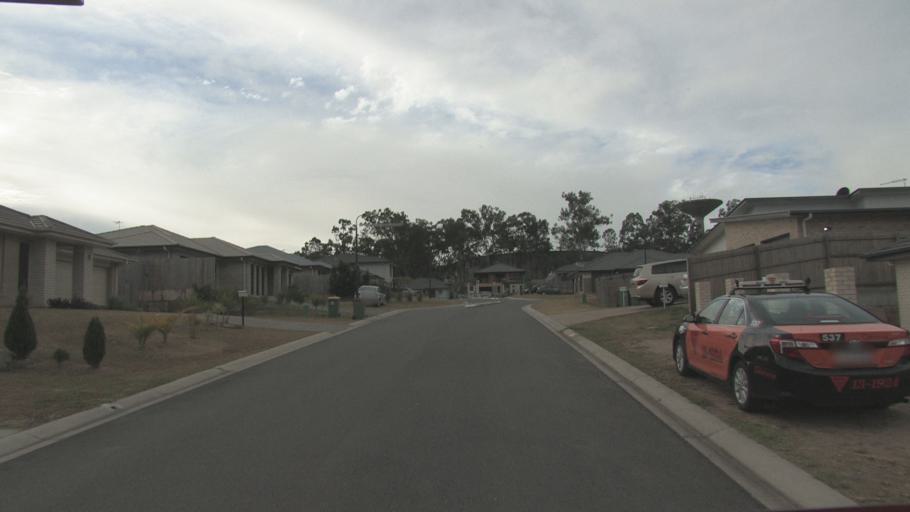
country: AU
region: Queensland
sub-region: Logan
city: Park Ridge South
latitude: -27.6794
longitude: 153.0284
